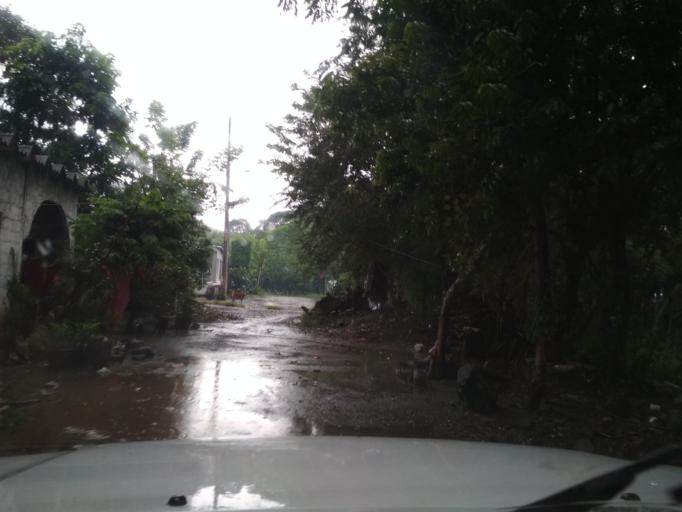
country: MX
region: Veracruz
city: Santiago Tuxtla
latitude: 18.4516
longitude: -95.3175
